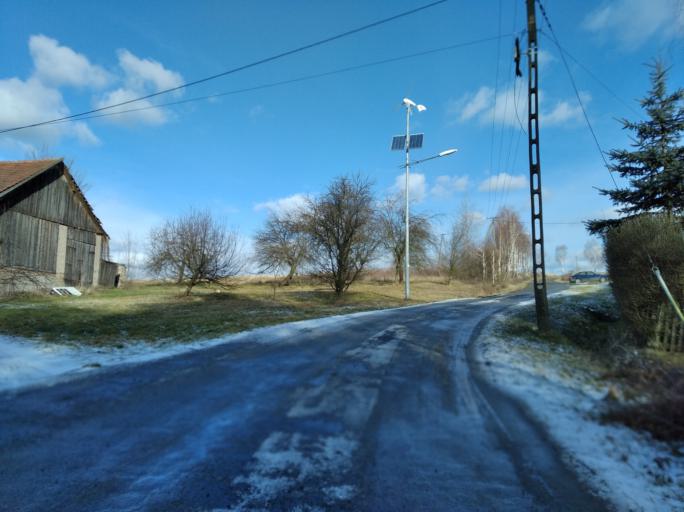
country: PL
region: Subcarpathian Voivodeship
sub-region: Powiat strzyzowski
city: Strzyzow
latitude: 49.9006
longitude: 21.7653
